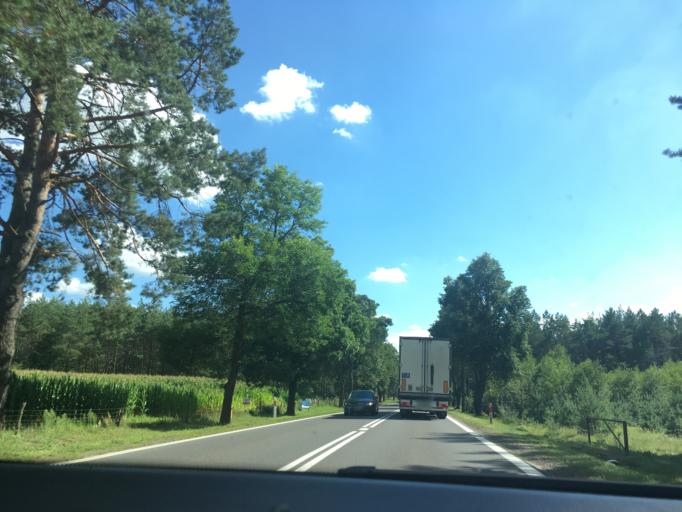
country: PL
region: Podlasie
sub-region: Powiat sokolski
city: Suchowola
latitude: 53.6432
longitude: 23.1197
